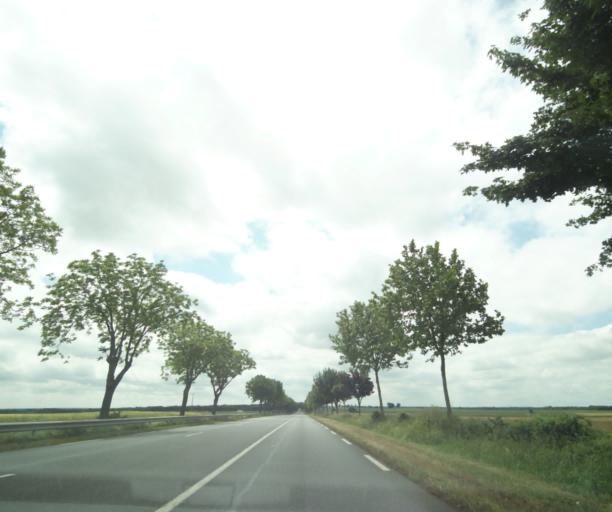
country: FR
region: Poitou-Charentes
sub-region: Departement des Deux-Sevres
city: Saint-Jean-de-Thouars
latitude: 46.9376
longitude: -0.2020
